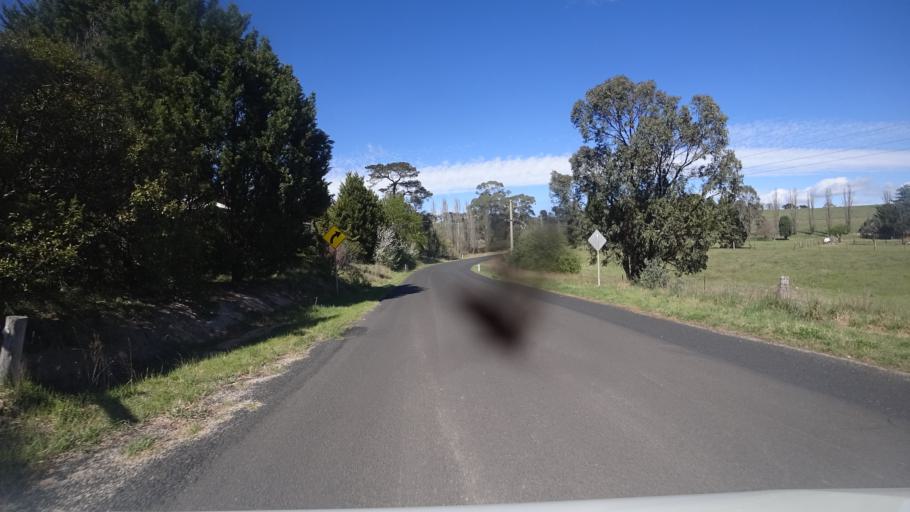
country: AU
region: New South Wales
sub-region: Lithgow
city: Bowenfels
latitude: -33.5160
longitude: 149.9941
